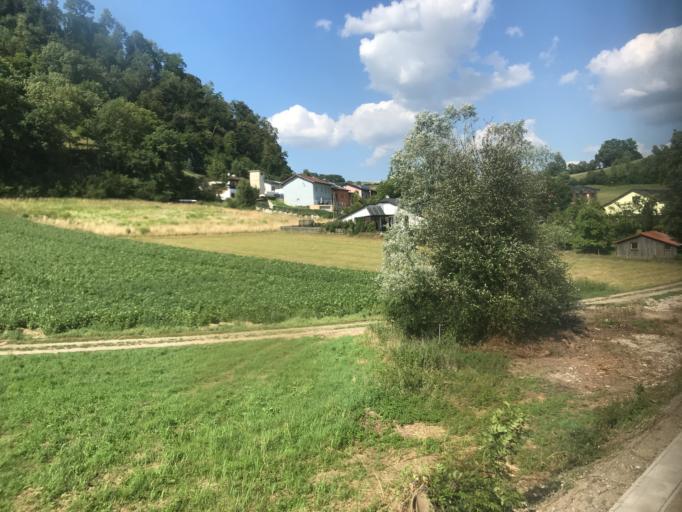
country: AT
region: Upper Austria
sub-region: Politischer Bezirk Linz-Land
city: Asten
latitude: 48.2604
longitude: 14.4147
